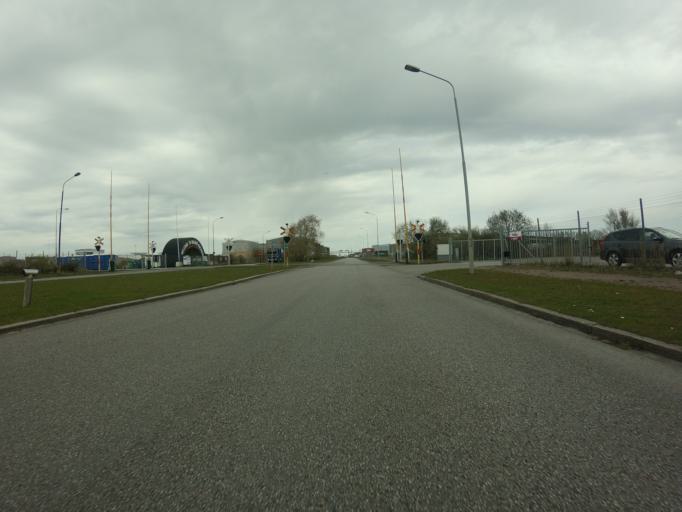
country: SE
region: Skane
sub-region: Burlovs Kommun
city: Arloev
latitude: 55.6306
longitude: 13.0362
